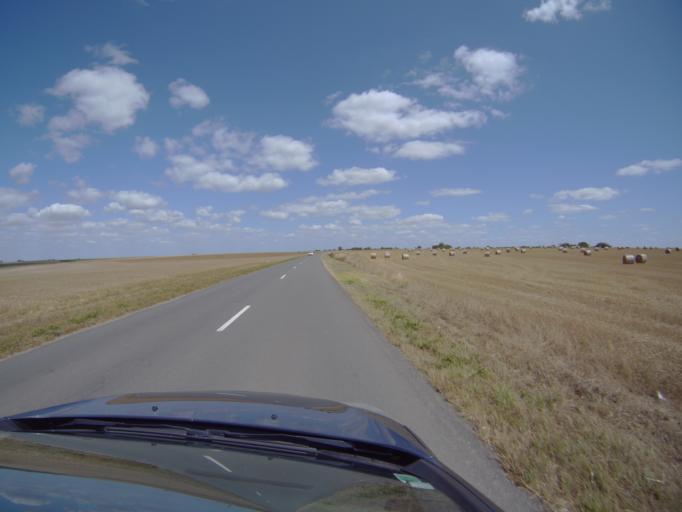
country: FR
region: Poitou-Charentes
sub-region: Departement des Deux-Sevres
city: Saint-Hilaire-la-Palud
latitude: 46.2642
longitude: -0.6868
